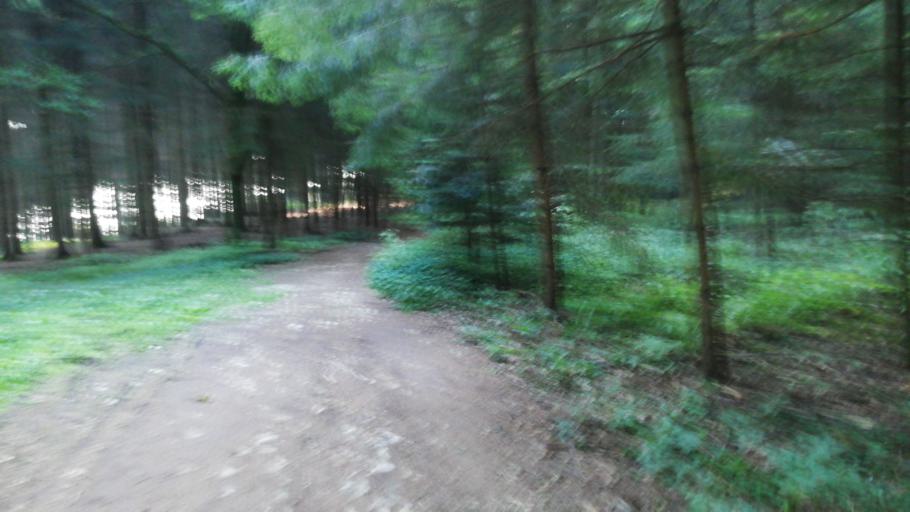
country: AT
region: Upper Austria
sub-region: Wels-Land
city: Gunskirchen
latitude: 48.1873
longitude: 13.9717
